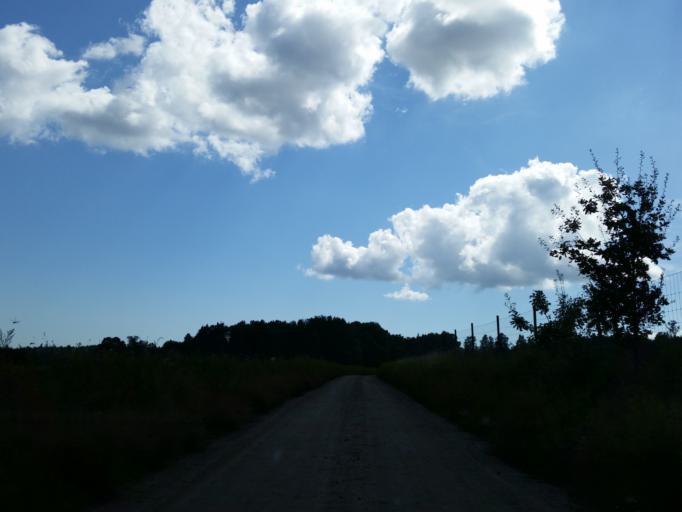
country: SE
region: Stockholm
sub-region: Sodertalje Kommun
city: Pershagen
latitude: 59.0659
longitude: 17.6612
